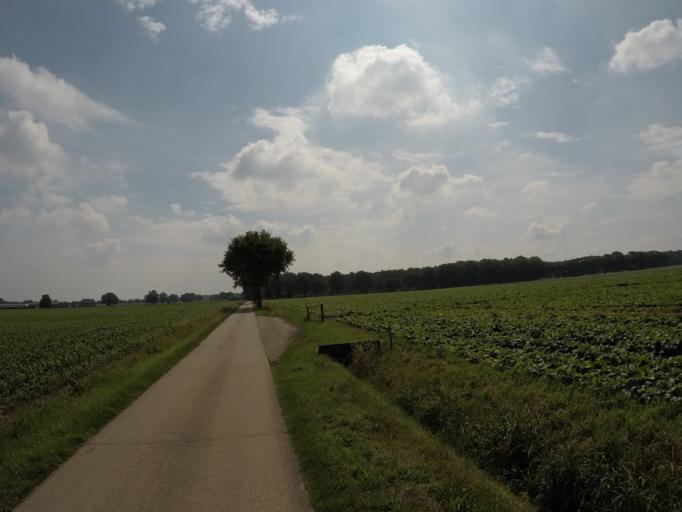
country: BE
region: Flanders
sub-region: Provincie Antwerpen
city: Brecht
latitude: 51.3339
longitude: 4.5849
